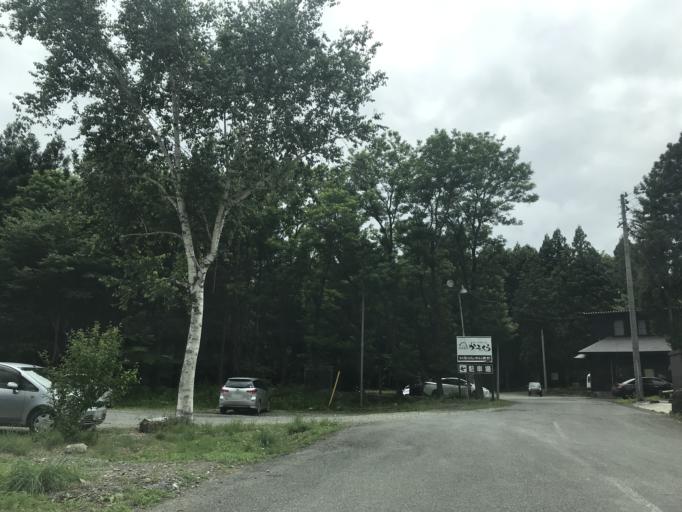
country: JP
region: Iwate
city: Ichinoseki
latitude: 39.0091
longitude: 140.8628
